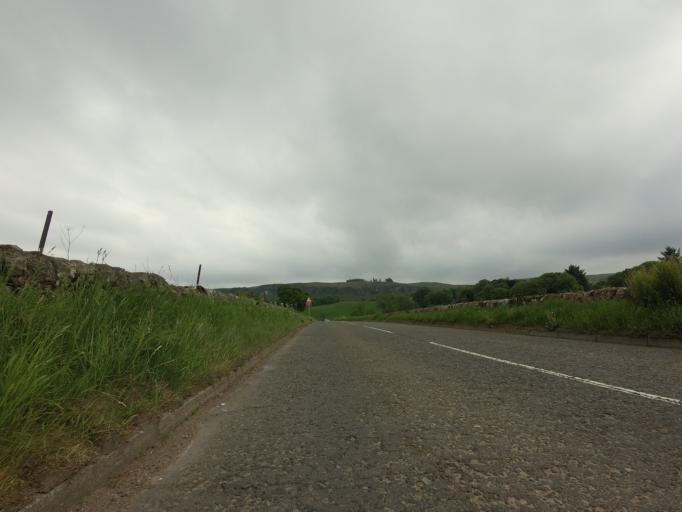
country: GB
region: Scotland
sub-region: Perth and Kinross
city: Kinross
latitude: 56.1656
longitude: -3.4473
